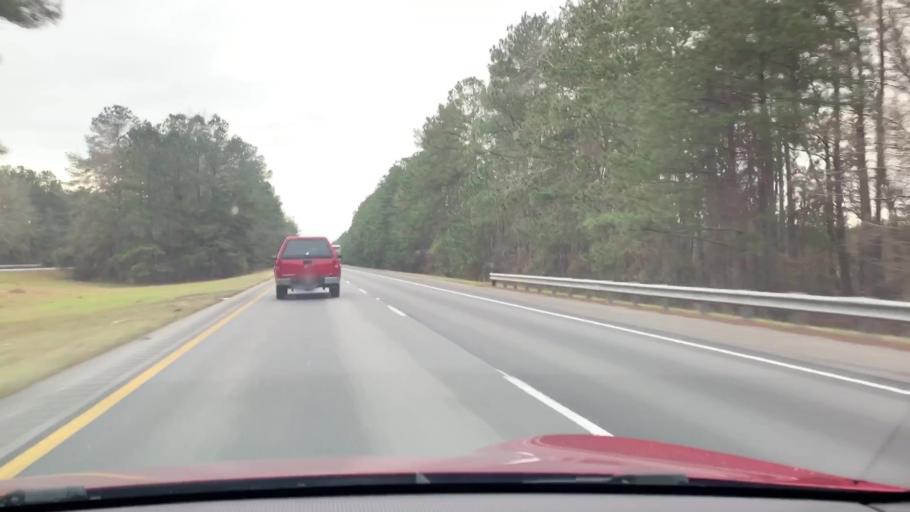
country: US
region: South Carolina
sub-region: Clarendon County
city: Manning
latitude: 33.6319
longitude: -80.2916
